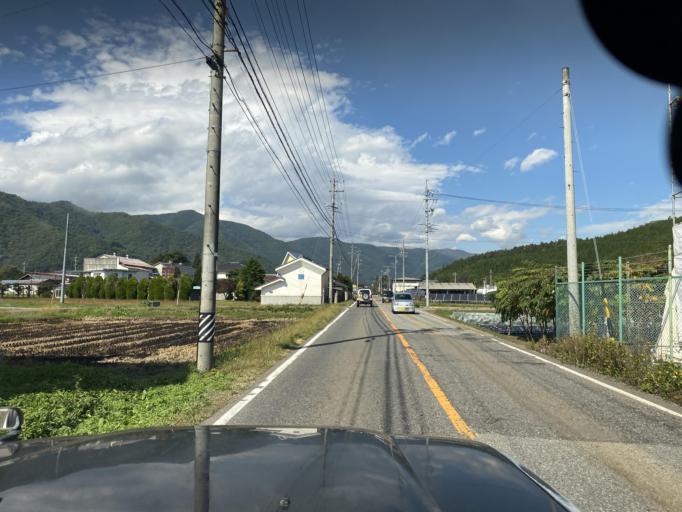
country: JP
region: Nagano
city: Omachi
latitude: 36.5334
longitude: 137.8465
